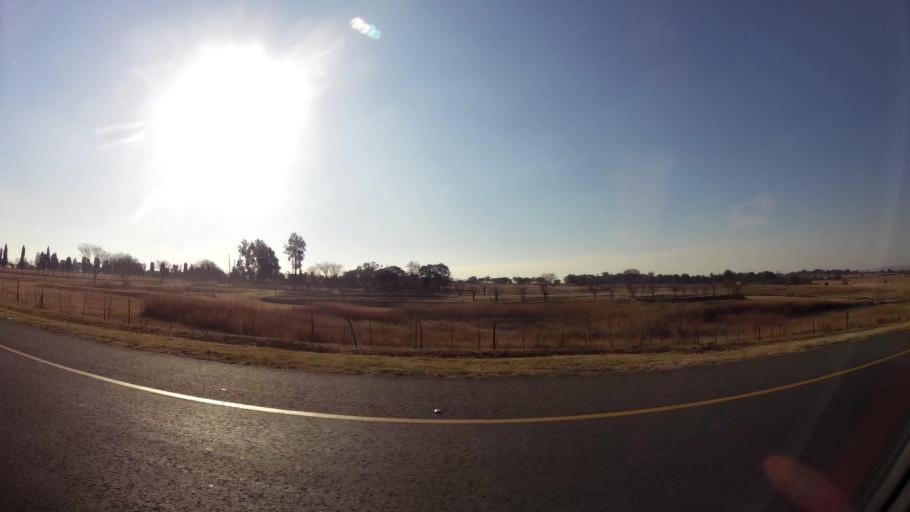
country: ZA
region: Gauteng
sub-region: West Rand District Municipality
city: Muldersdriseloop
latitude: -26.0105
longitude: 27.8848
